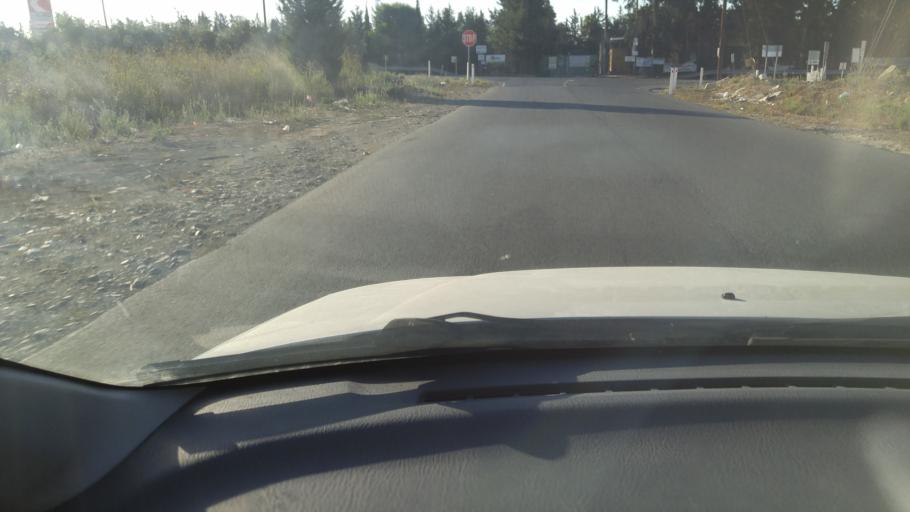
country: CY
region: Limassol
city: Ypsonas
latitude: 34.6545
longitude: 32.9750
